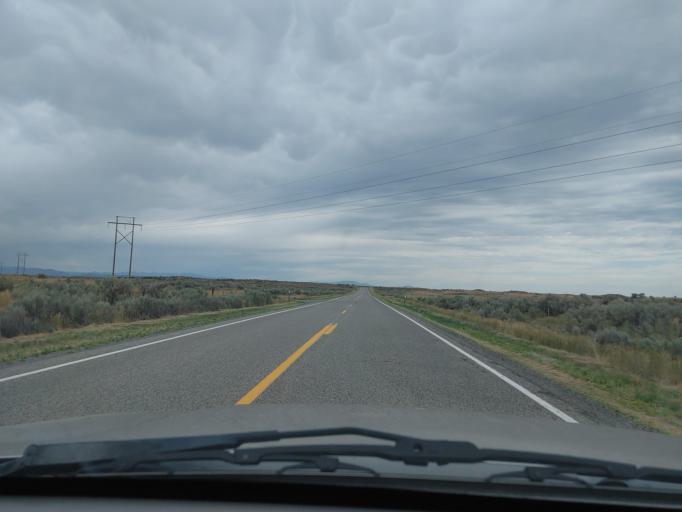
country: US
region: Idaho
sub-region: Lincoln County
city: Shoshone
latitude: 43.0870
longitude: -114.0953
